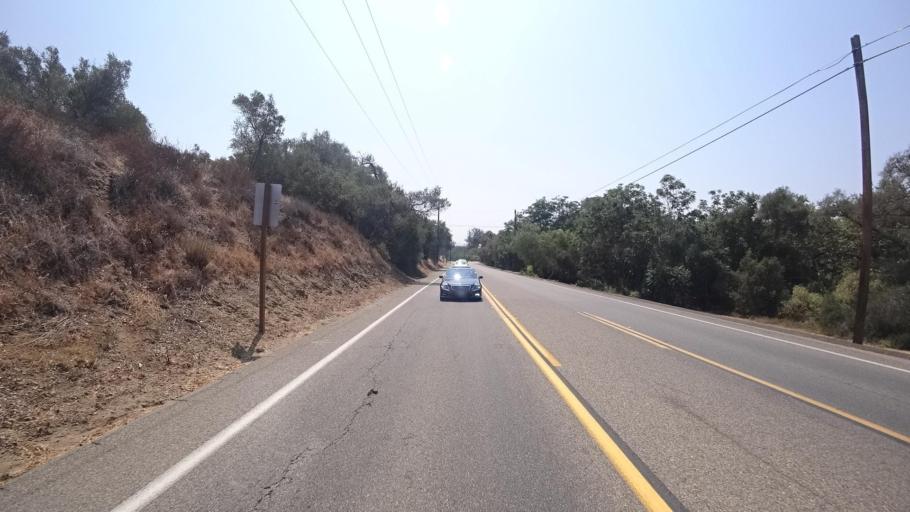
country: US
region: California
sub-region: San Diego County
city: Fallbrook
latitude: 33.3408
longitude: -117.2392
